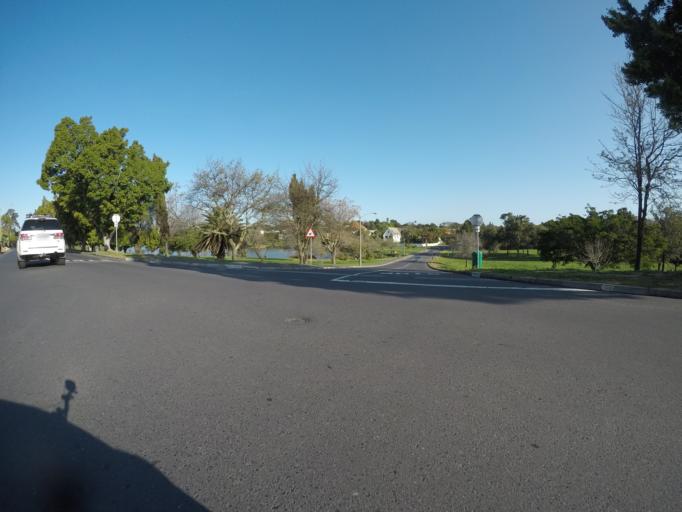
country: ZA
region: Western Cape
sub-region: City of Cape Town
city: Kraaifontein
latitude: -33.8469
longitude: 18.6593
